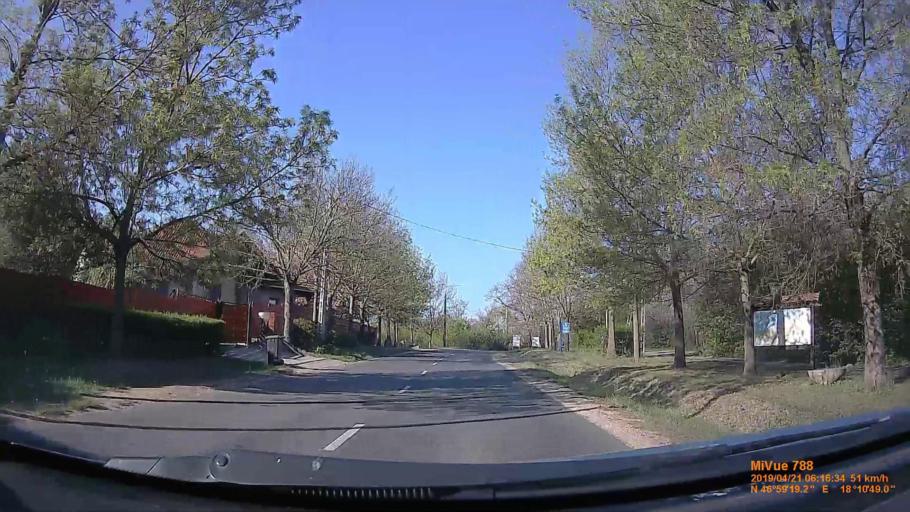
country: HU
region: Fejer
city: Lepseny
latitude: 46.9886
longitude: 18.1803
